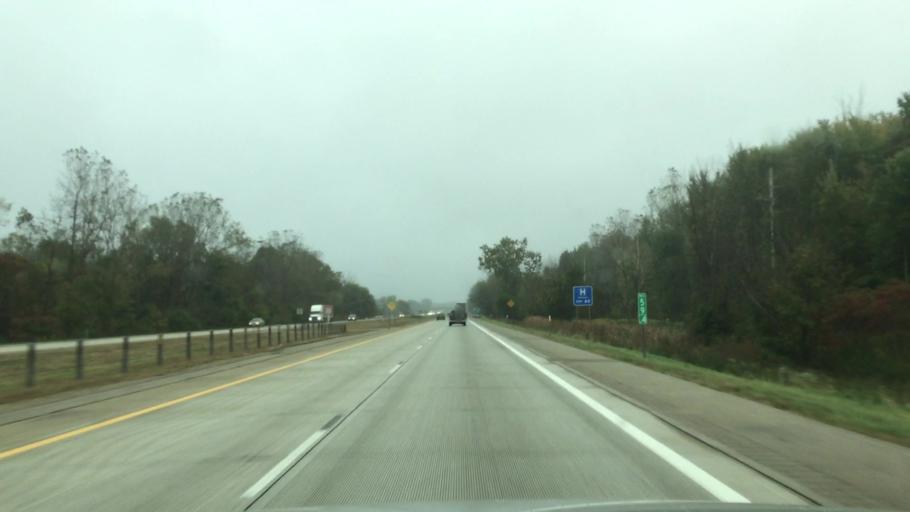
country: US
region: Michigan
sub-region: Van Buren County
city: Paw Paw
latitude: 42.2054
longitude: -85.9069
